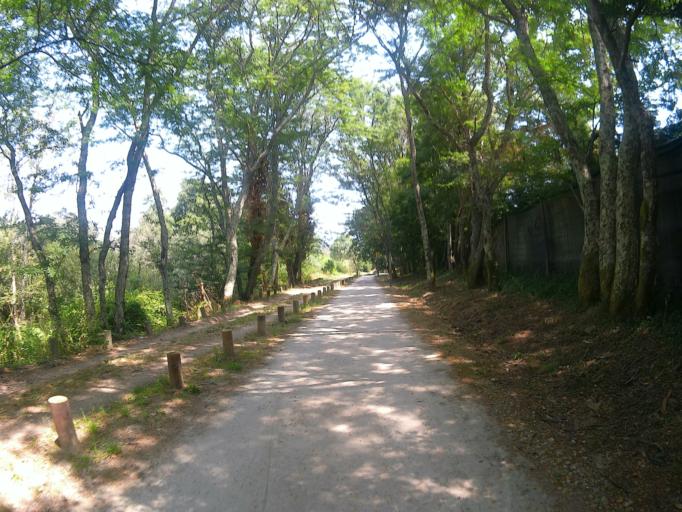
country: PT
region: Viana do Castelo
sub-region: Ponte de Lima
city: Ponte de Lima
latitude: 41.7736
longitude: -8.5834
